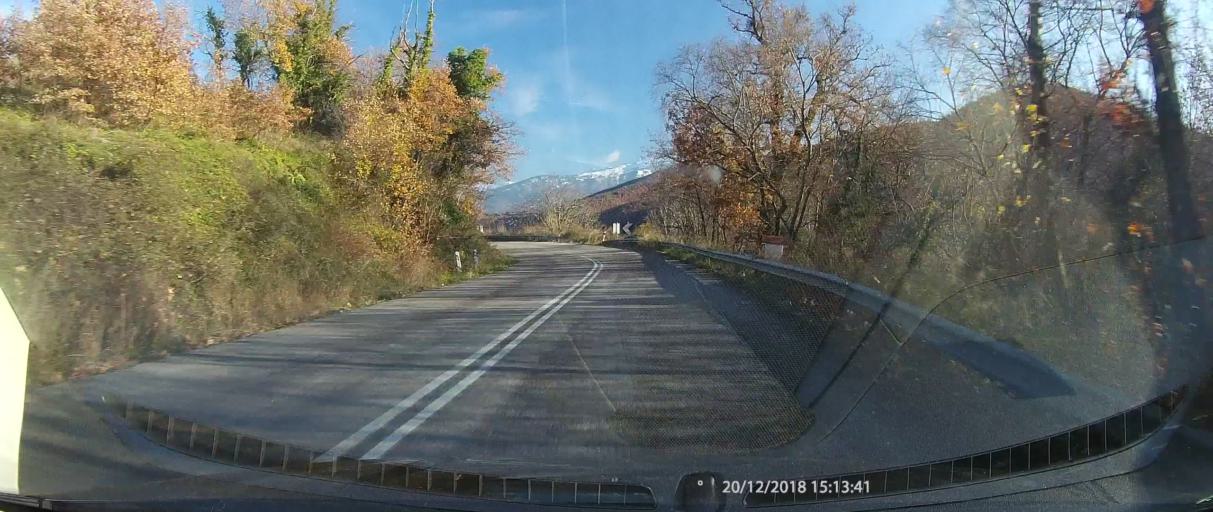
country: GR
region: Central Greece
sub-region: Nomos Fthiotidos
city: Makrakomi
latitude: 38.9321
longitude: 21.9711
